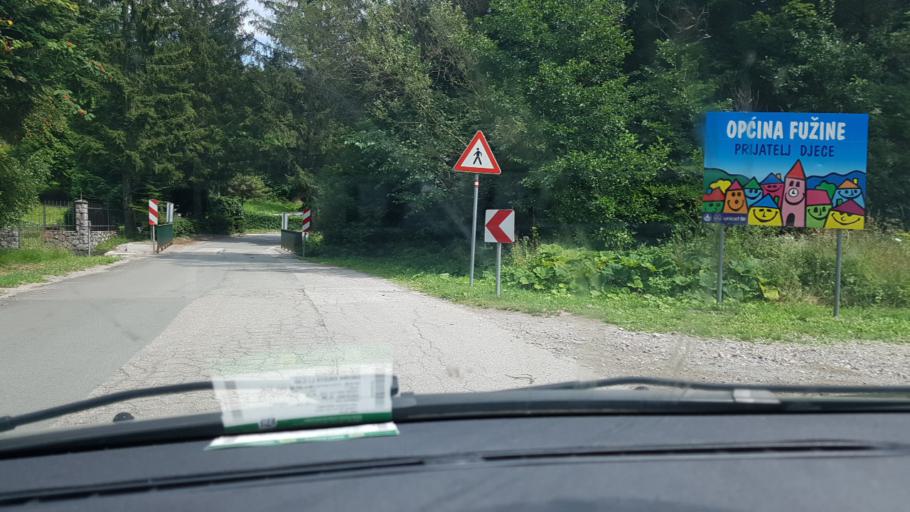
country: HR
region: Primorsko-Goranska
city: Hreljin
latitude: 45.3278
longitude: 14.7011
